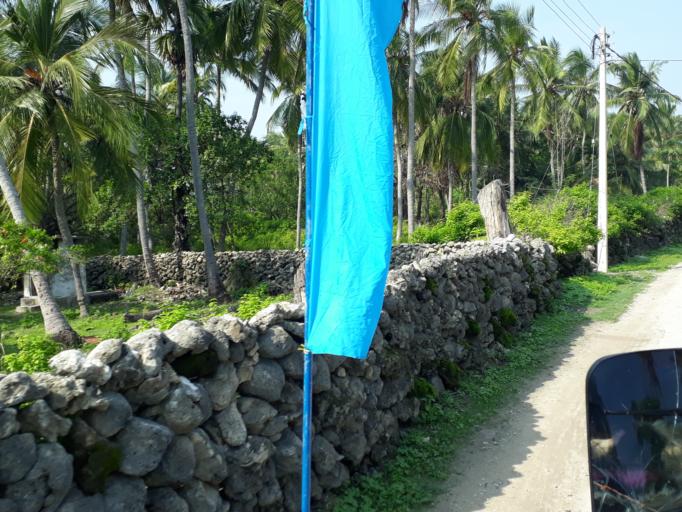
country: LK
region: Northern Province
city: Jaffna
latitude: 9.5275
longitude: 79.7112
